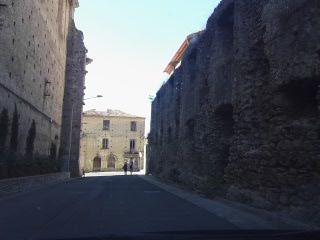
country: IT
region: Calabria
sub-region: Provincia di Vibo-Valentia
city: Sorianello
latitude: 38.5966
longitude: 16.2312
